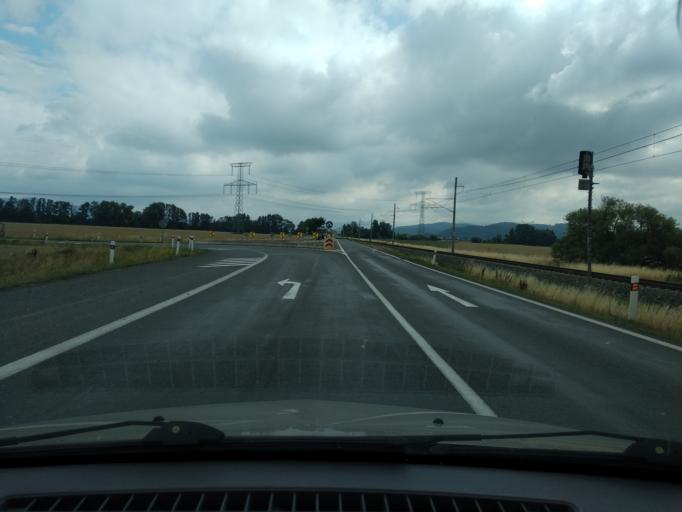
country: CZ
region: Olomoucky
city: Postrelmov
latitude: 49.8933
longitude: 16.8976
